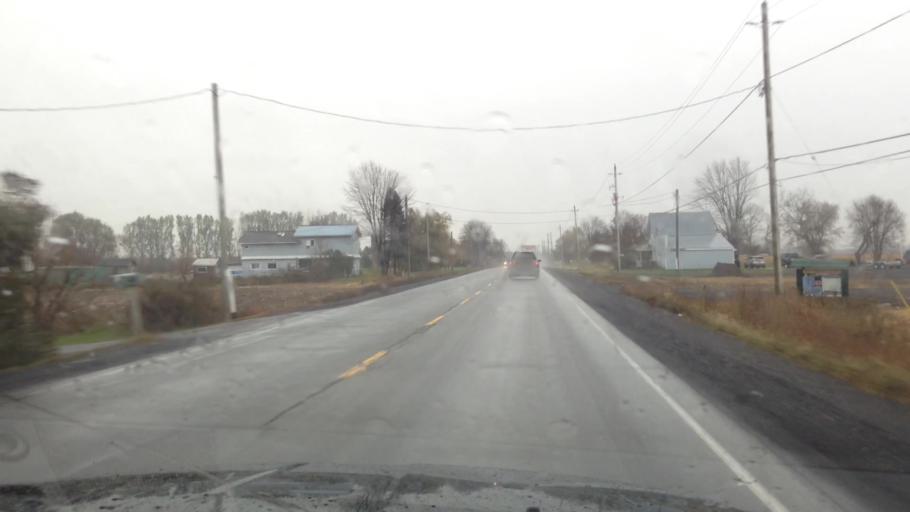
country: CA
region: Ontario
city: Bourget
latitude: 45.3204
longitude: -75.3400
